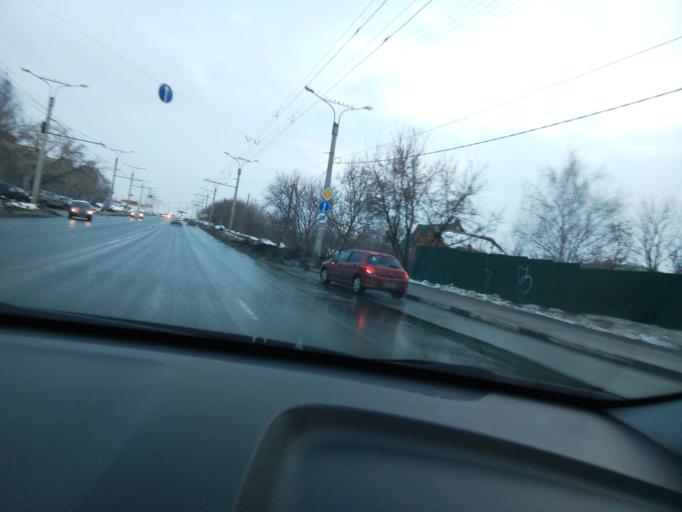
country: RU
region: Chuvashia
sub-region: Cheboksarskiy Rayon
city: Cheboksary
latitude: 56.1273
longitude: 47.2437
